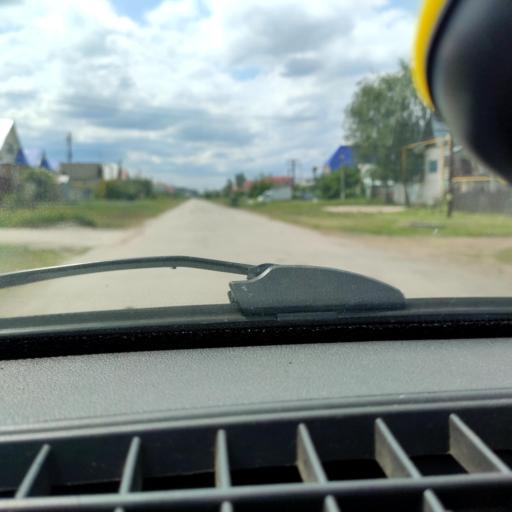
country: RU
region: Samara
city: Povolzhskiy
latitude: 53.6409
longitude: 49.6857
